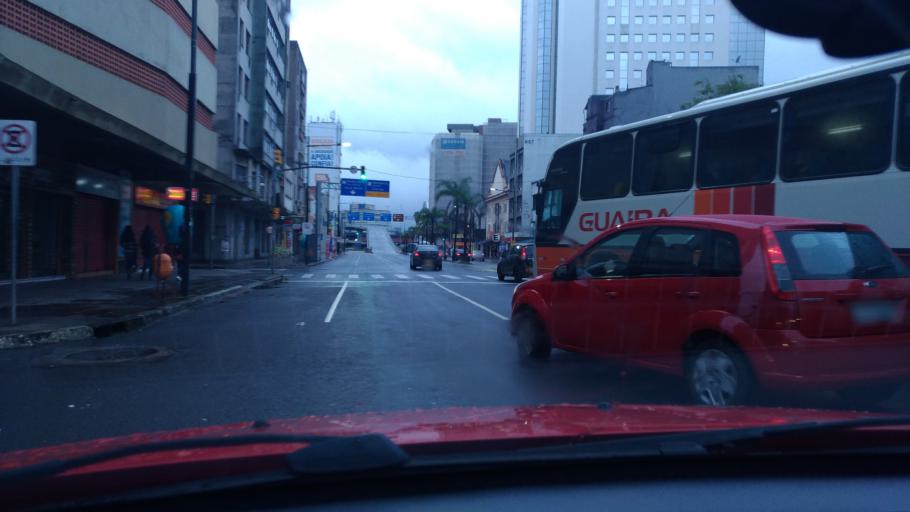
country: BR
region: Rio Grande do Sul
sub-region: Porto Alegre
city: Porto Alegre
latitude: -30.0251
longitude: -51.2233
